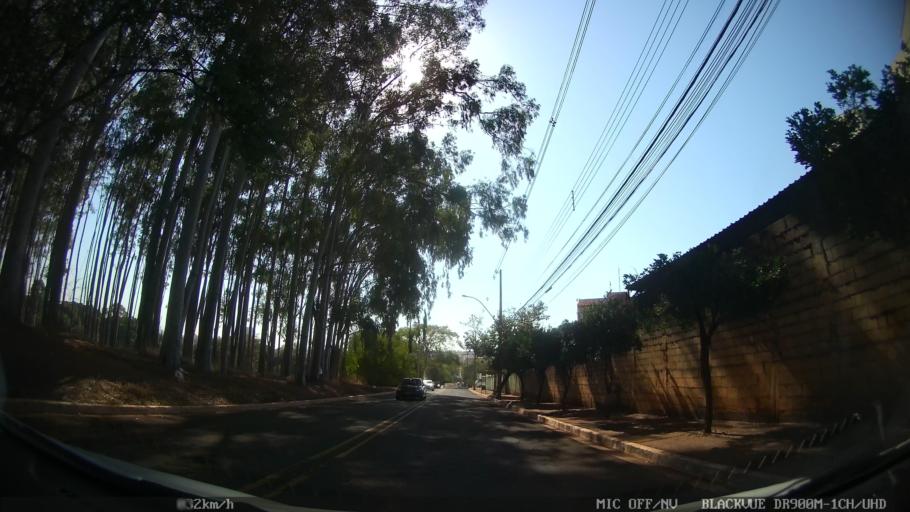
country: BR
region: Sao Paulo
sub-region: Ribeirao Preto
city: Ribeirao Preto
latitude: -21.2111
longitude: -47.8260
